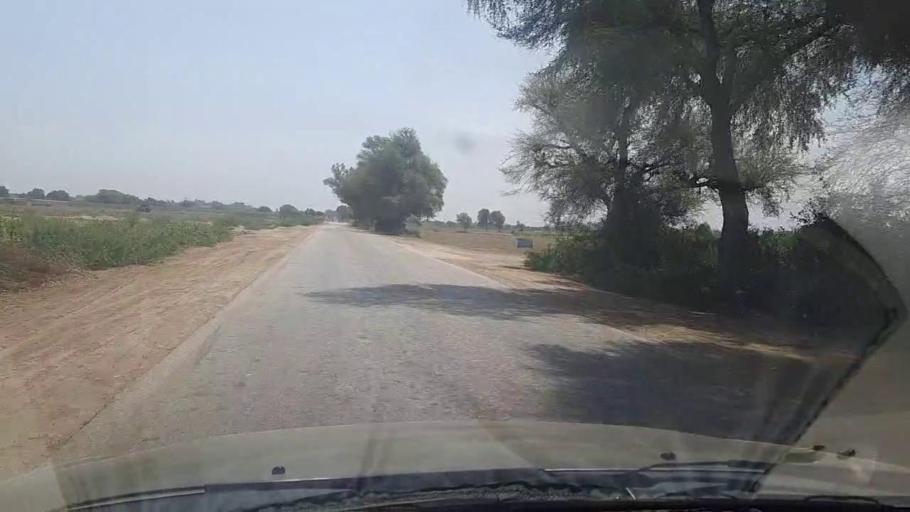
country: PK
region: Sindh
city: Tando Jam
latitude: 25.3754
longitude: 68.4630
